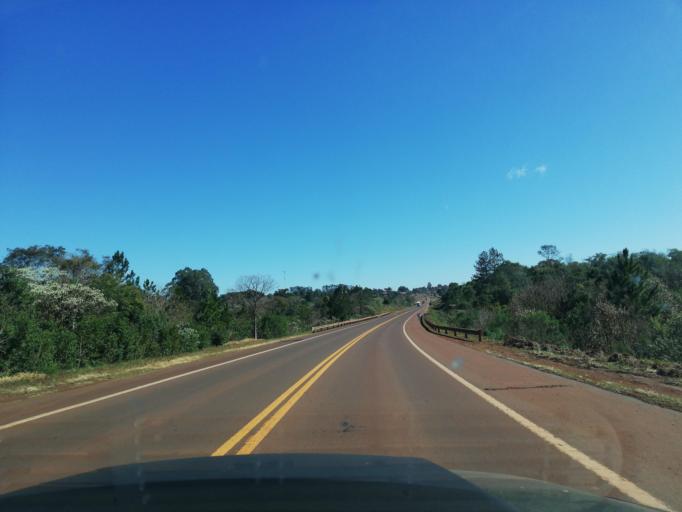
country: AR
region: Misiones
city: Aristobulo del Valle
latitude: -27.0984
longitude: -54.8759
